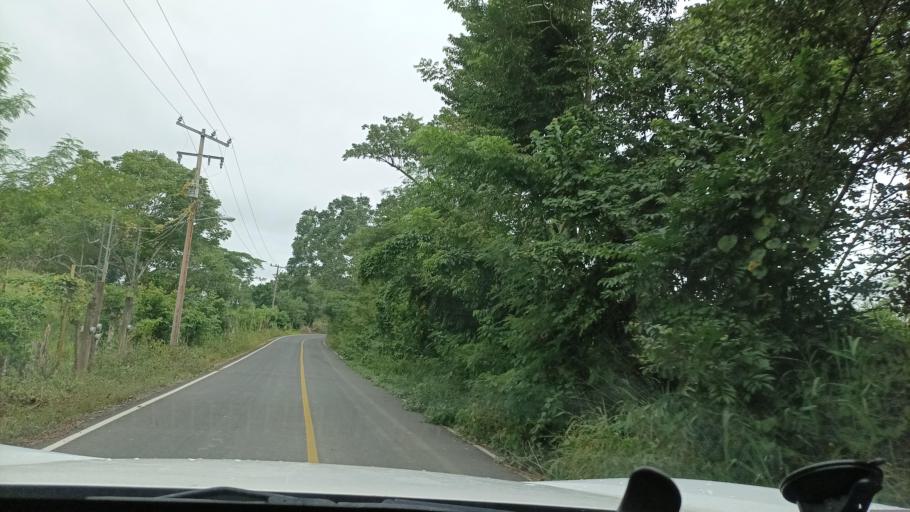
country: MX
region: Veracruz
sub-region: Moloacan
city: Cuichapa
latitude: 17.7940
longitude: -94.3579
